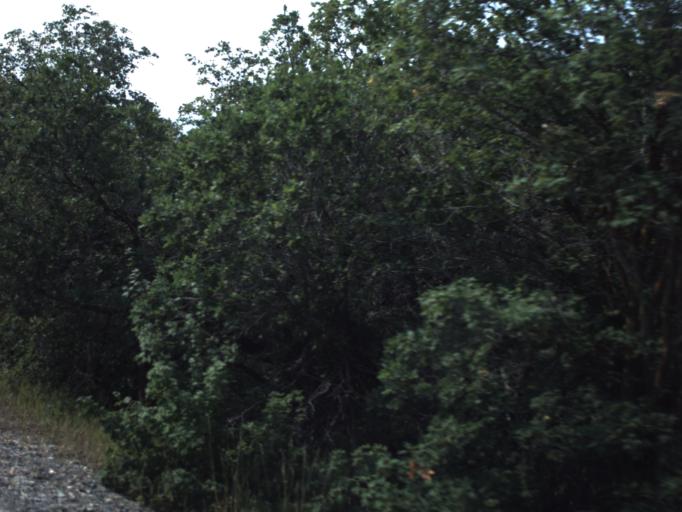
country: US
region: Utah
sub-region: Summit County
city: Summit Park
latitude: 40.8102
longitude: -111.6783
